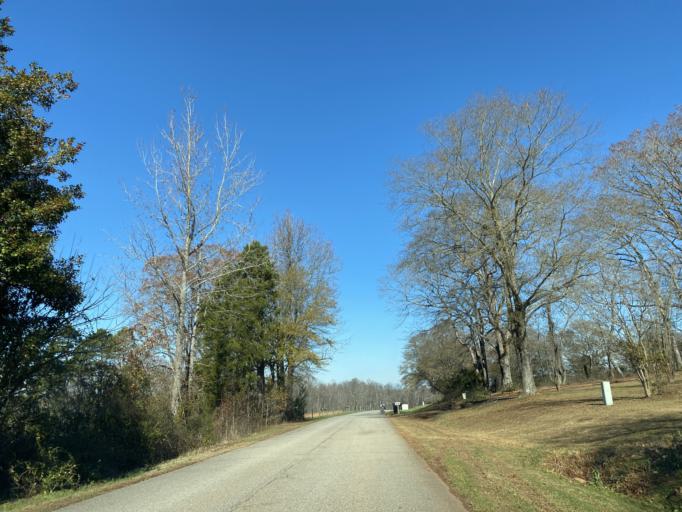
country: US
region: South Carolina
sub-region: Spartanburg County
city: Mayo
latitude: 35.1384
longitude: -81.7858
